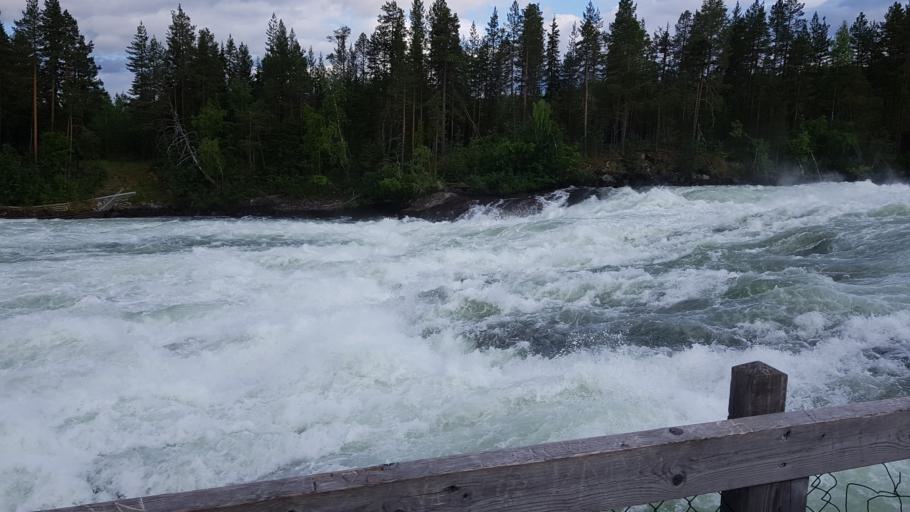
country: SE
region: Norrbotten
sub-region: Alvsbyns Kommun
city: AElvsbyn
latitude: 65.8503
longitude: 20.4061
